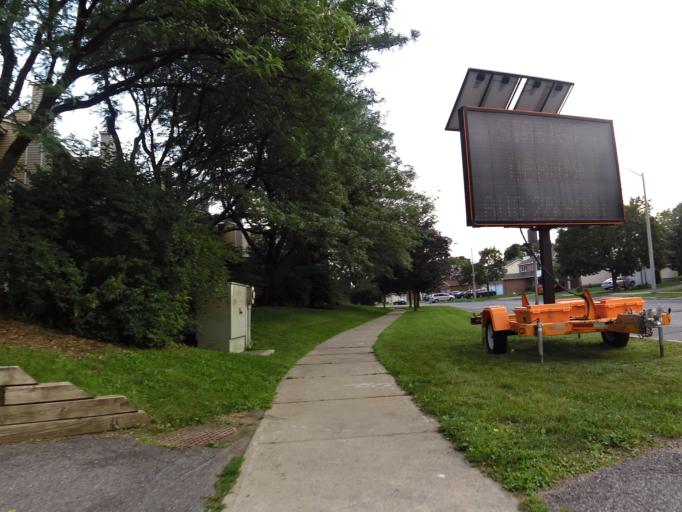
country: CA
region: Ontario
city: Bells Corners
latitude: 45.3688
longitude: -75.7697
